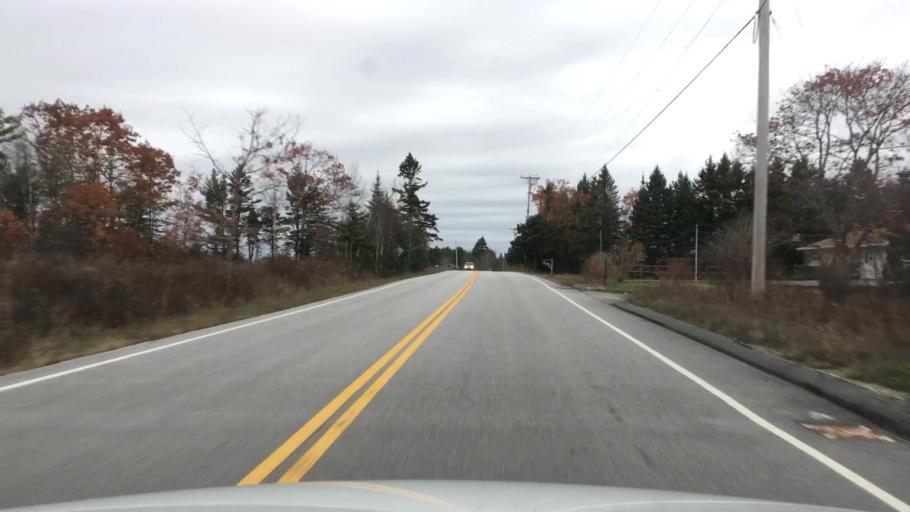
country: US
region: Maine
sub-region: Hancock County
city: Orland
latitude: 44.5314
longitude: -68.6754
